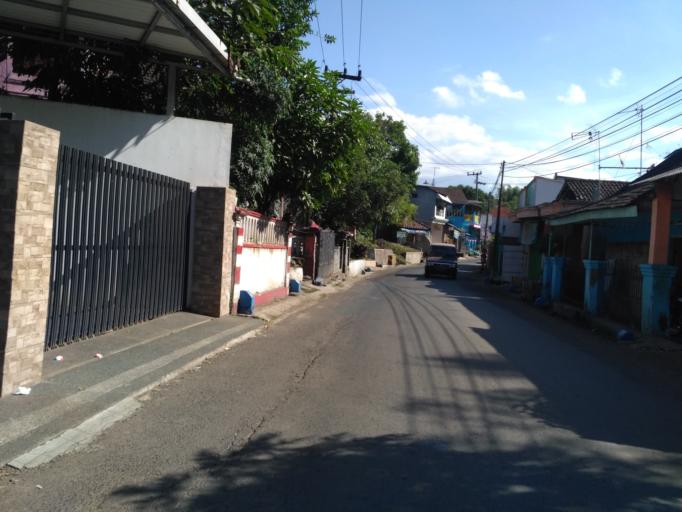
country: ID
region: East Java
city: Singosari
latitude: -7.9152
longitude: 112.6600
